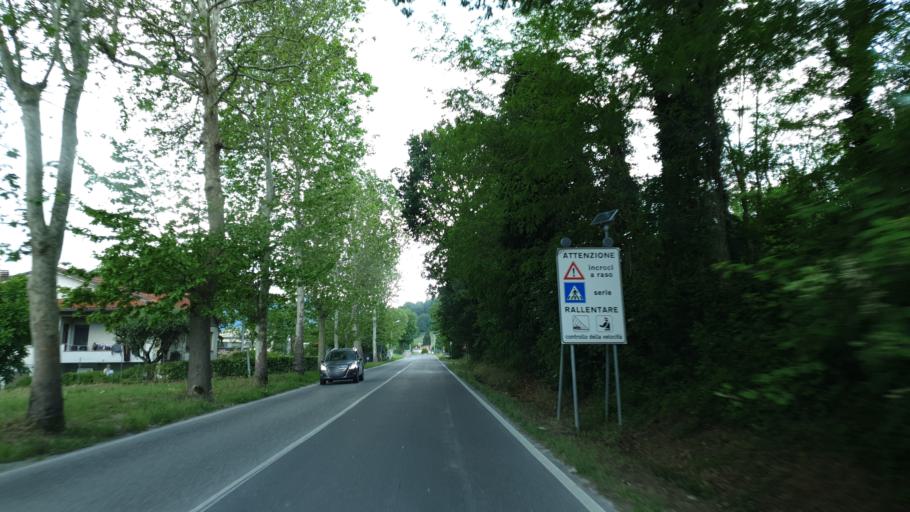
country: IT
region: Emilia-Romagna
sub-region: Provincia di Rimini
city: Secchiano
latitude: 43.9314
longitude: 12.3291
